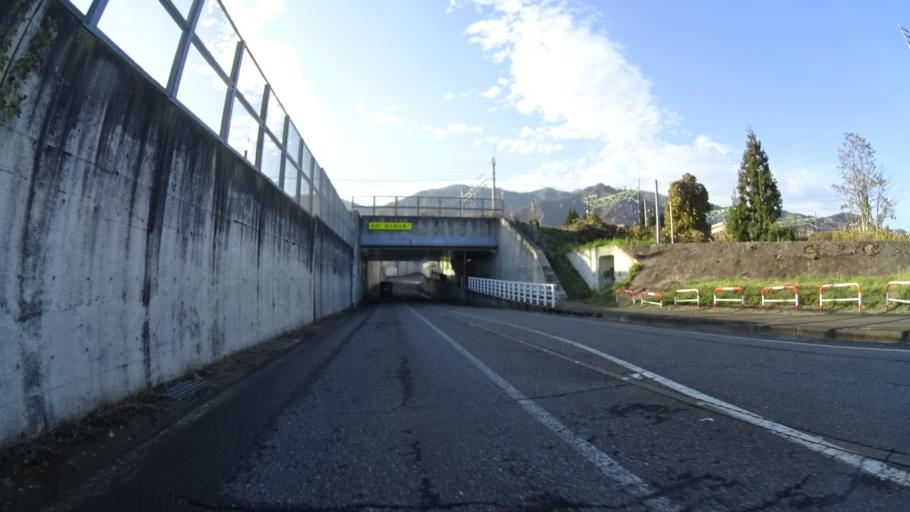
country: JP
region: Niigata
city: Shiozawa
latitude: 36.9852
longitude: 138.8045
